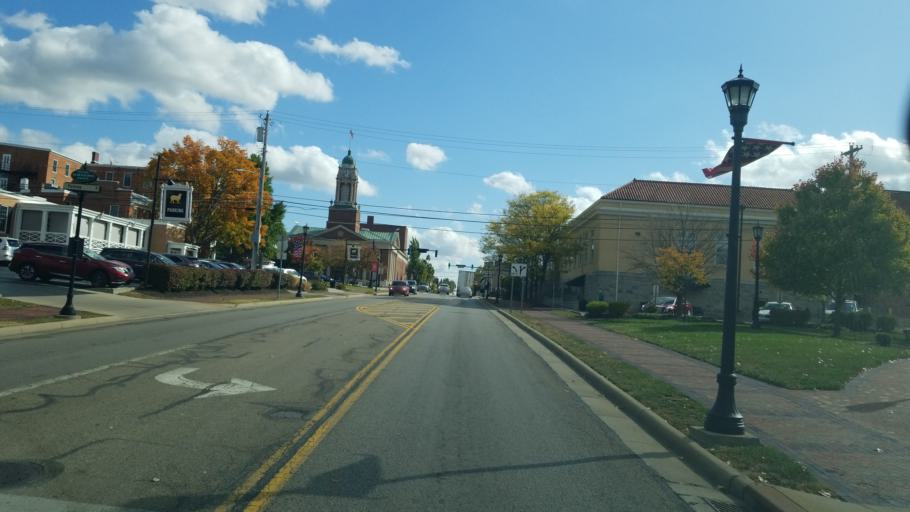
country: US
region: Ohio
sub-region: Warren County
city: Lebanon
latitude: 39.4334
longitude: -84.2101
